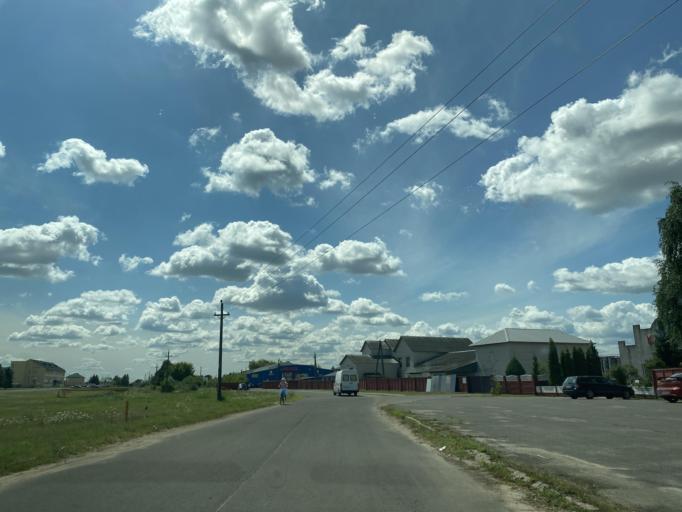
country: BY
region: Brest
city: Ivanava
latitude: 52.1393
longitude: 25.5522
